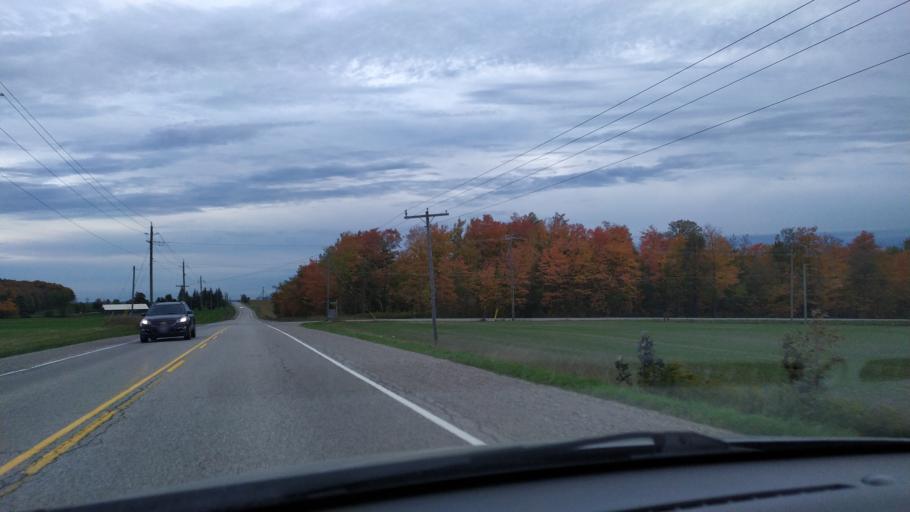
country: CA
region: Ontario
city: Stratford
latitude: 43.5099
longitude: -80.7577
